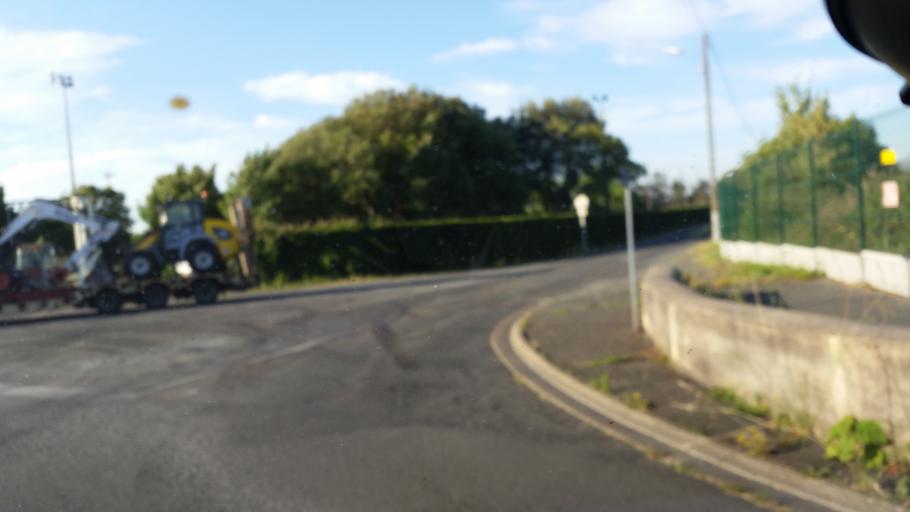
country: FR
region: Poitou-Charentes
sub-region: Departement de la Charente-Maritime
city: Marans
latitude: 46.3036
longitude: -0.9938
